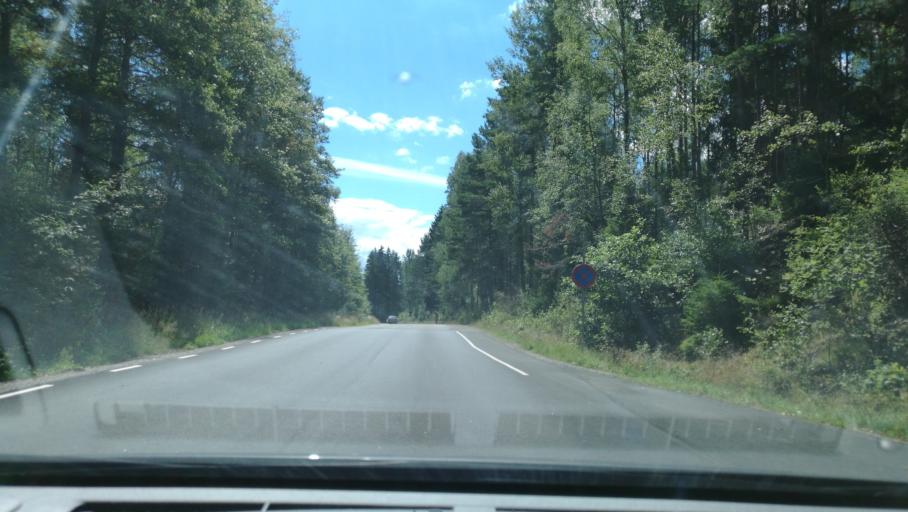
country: SE
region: OEstergoetland
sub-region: Norrkopings Kommun
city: Krokek
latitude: 58.6644
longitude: 16.4681
